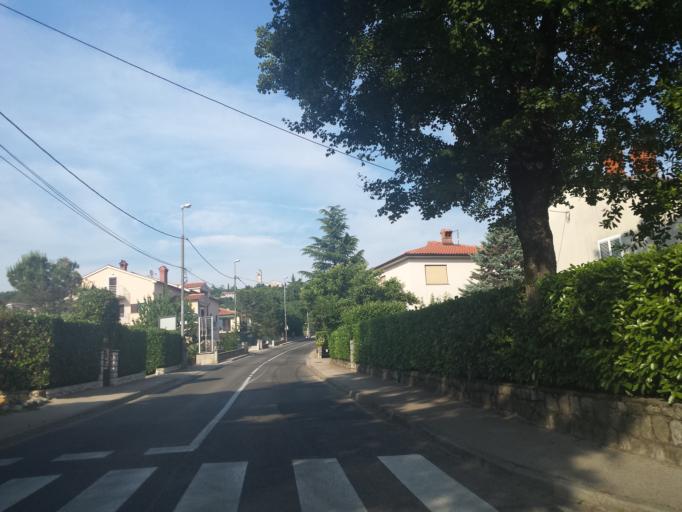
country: HR
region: Primorsko-Goranska
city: Rubesi
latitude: 45.3703
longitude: 14.3395
